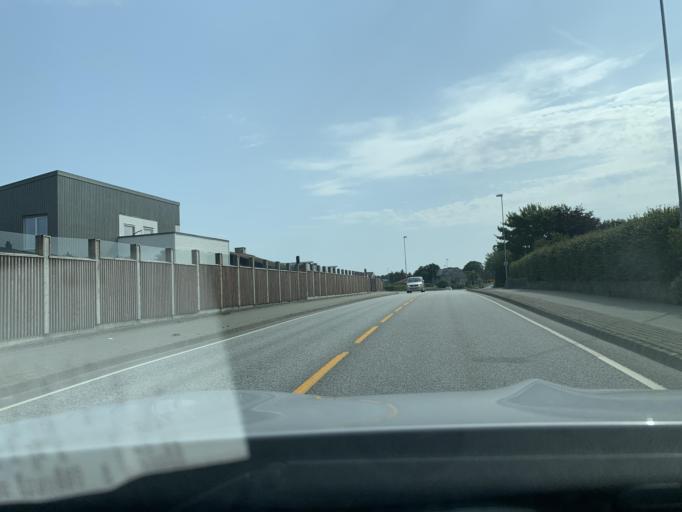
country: NO
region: Rogaland
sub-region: Klepp
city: Kleppe
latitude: 58.7689
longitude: 5.6294
